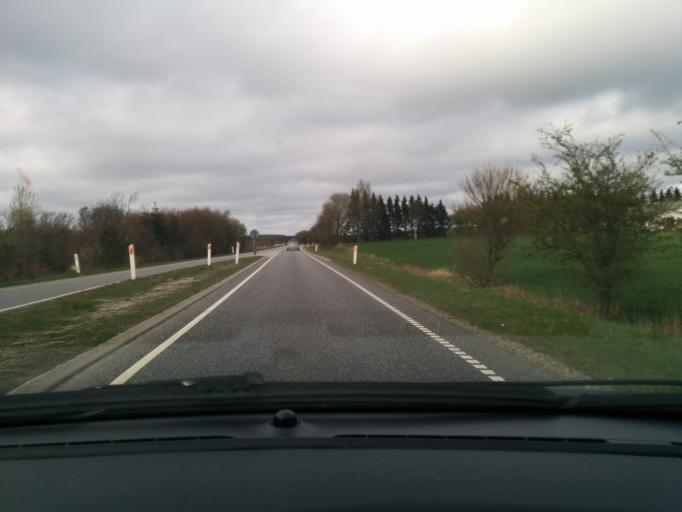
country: DK
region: Central Jutland
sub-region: Favrskov Kommune
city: Hammel
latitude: 56.2361
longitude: 9.8666
